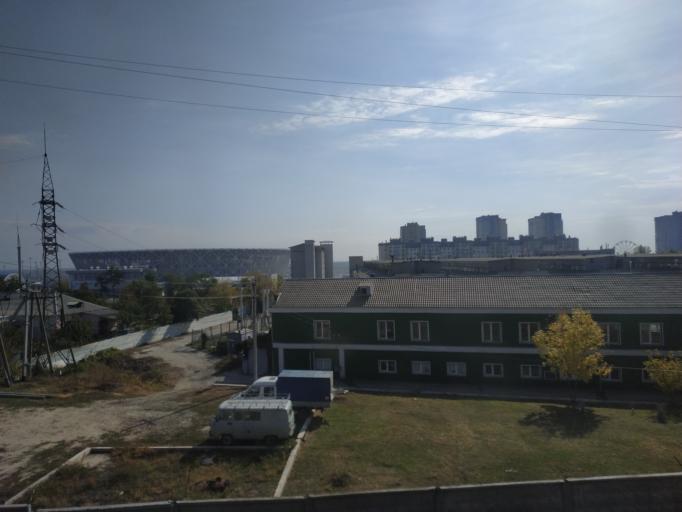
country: RU
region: Volgograd
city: Volgograd
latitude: 48.7354
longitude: 44.5392
